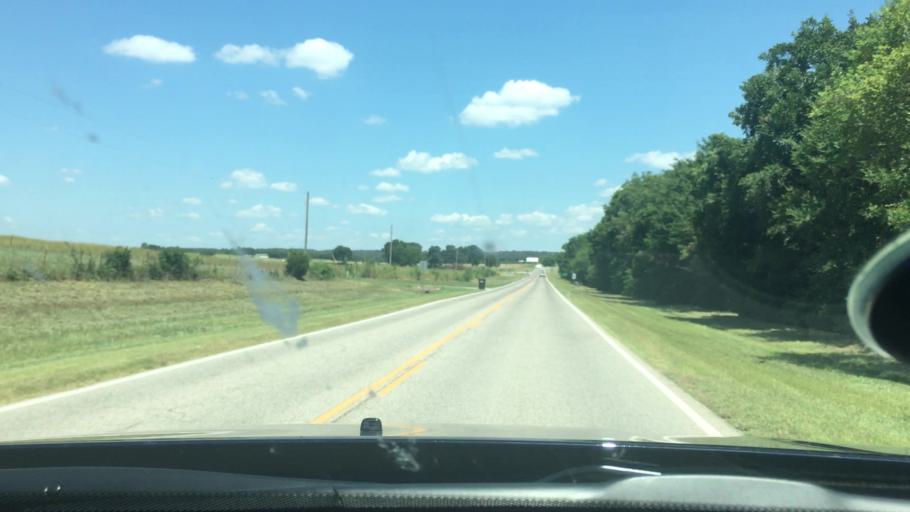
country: US
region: Oklahoma
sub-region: Carter County
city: Dickson
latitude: 34.2844
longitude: -96.9683
